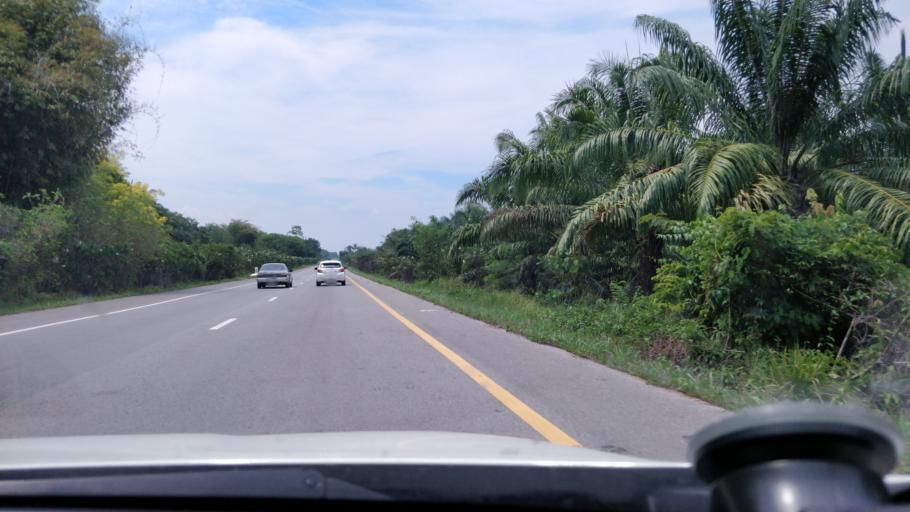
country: TH
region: Surat Thani
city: Khian Sa
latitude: 8.7756
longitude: 99.1613
